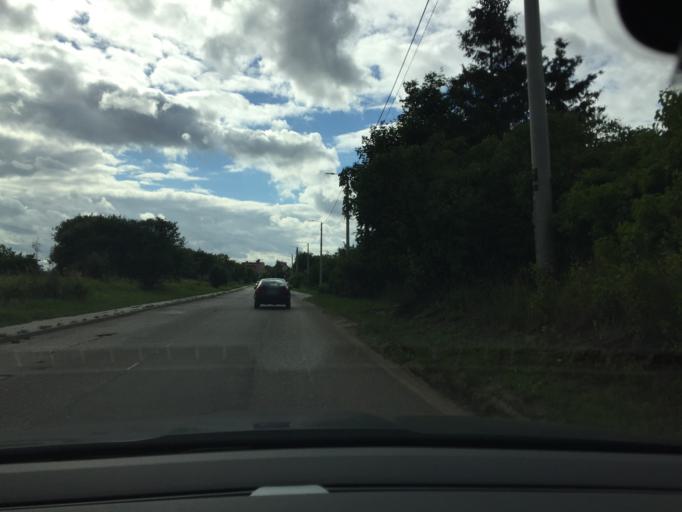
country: PL
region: Pomeranian Voivodeship
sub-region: Gdansk
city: Gdansk
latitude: 54.3594
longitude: 18.7444
